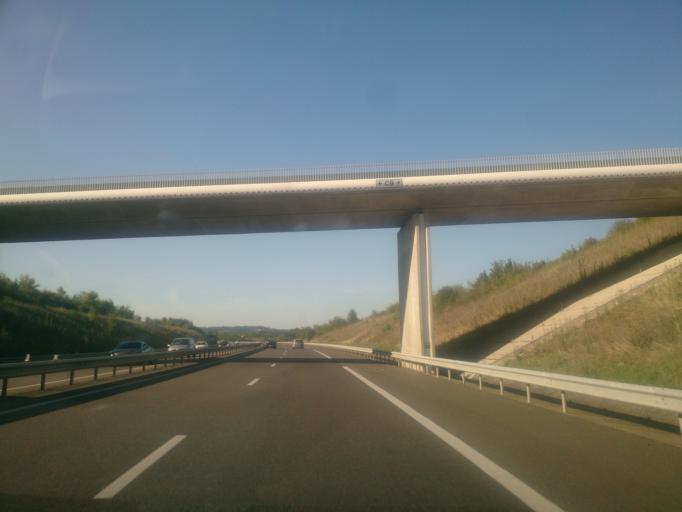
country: FR
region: Midi-Pyrenees
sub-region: Departement du Tarn-et-Garonne
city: Caussade
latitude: 44.2066
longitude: 1.5419
